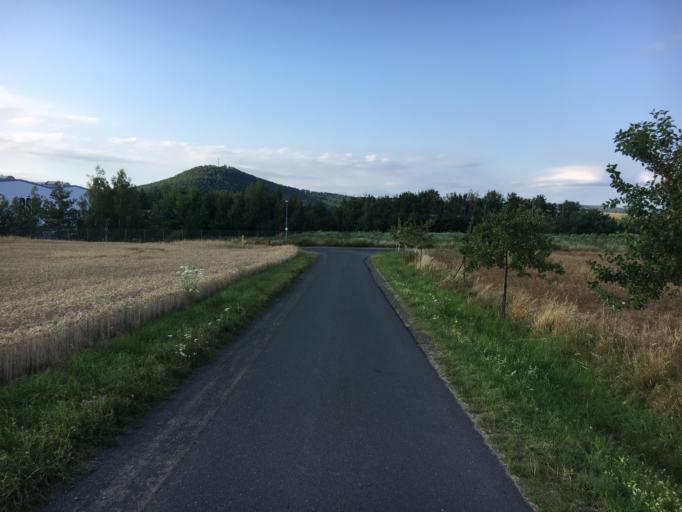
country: DE
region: Thuringia
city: Stadtlengsfeld
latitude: 50.8157
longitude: 10.1307
